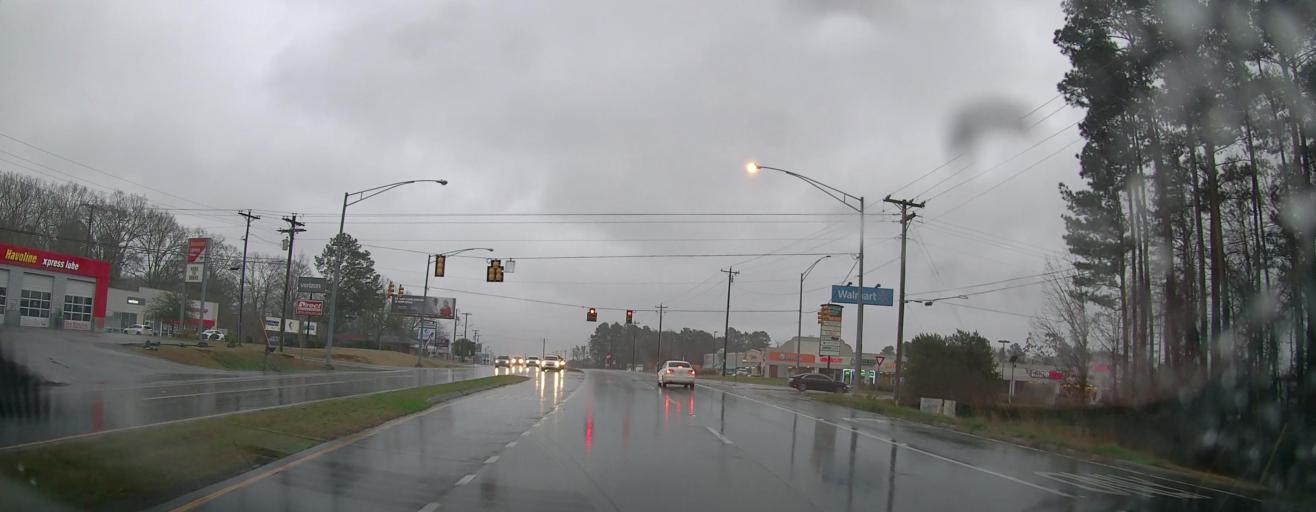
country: US
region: Alabama
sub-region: Morgan County
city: Hartselle
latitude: 34.4538
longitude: -86.9469
